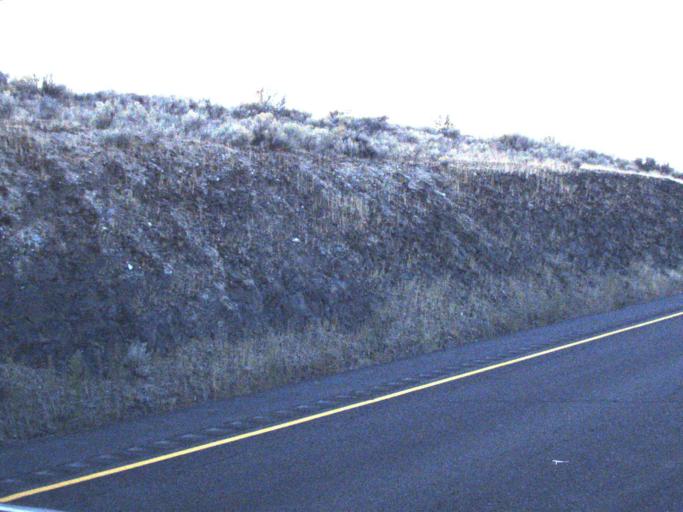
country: US
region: Washington
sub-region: Adams County
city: Ritzville
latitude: 47.0349
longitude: -118.4597
